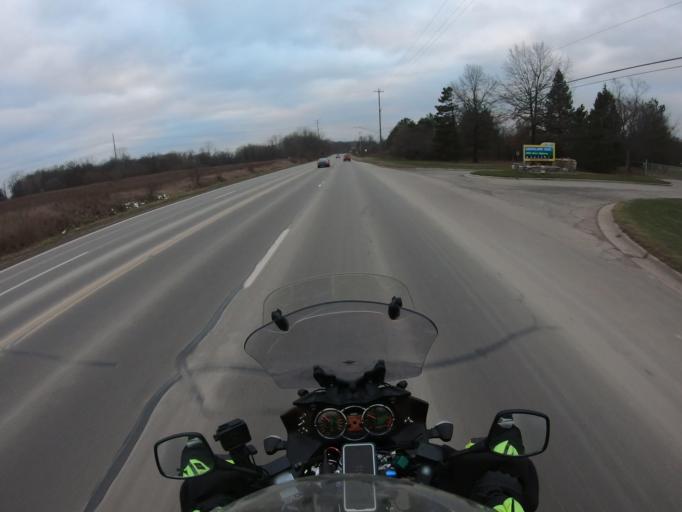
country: US
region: Michigan
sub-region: Oakland County
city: Holly
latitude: 42.8187
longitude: -83.5515
